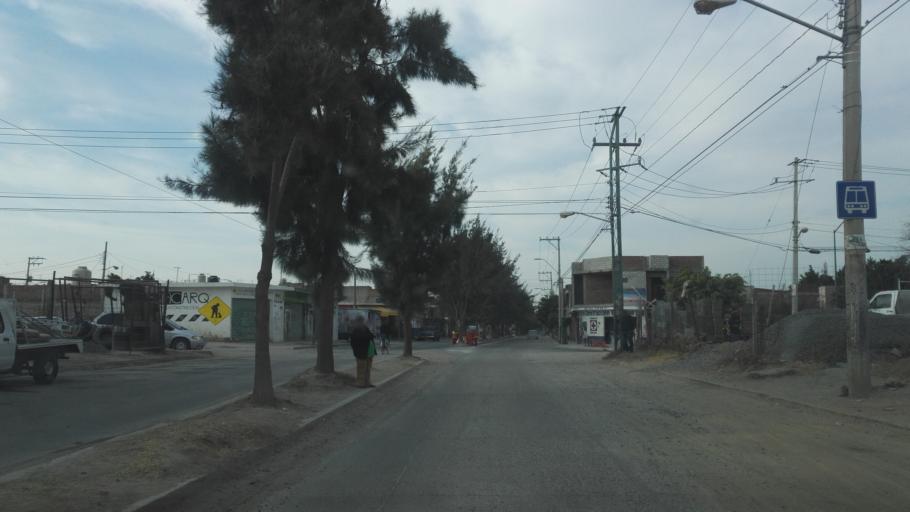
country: MX
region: Guanajuato
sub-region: Leon
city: Fraccionamiento Paraiso Real
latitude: 21.1002
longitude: -101.6016
